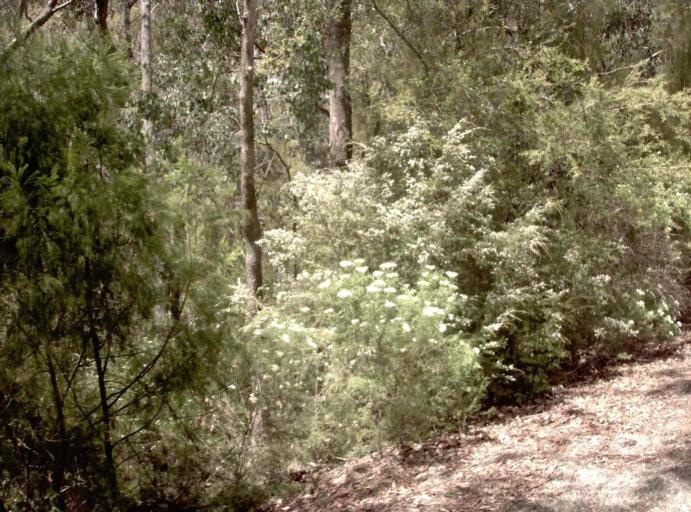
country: AU
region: Victoria
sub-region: East Gippsland
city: Lakes Entrance
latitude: -37.5802
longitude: 147.8950
